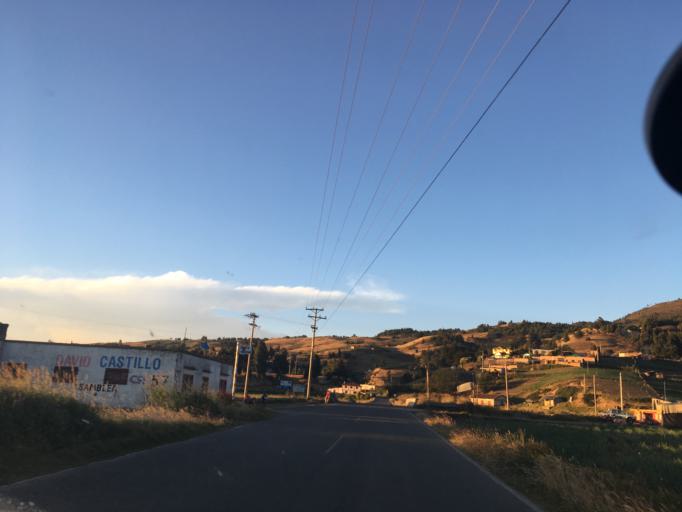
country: CO
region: Boyaca
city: Aquitania
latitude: 5.5570
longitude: -72.8798
